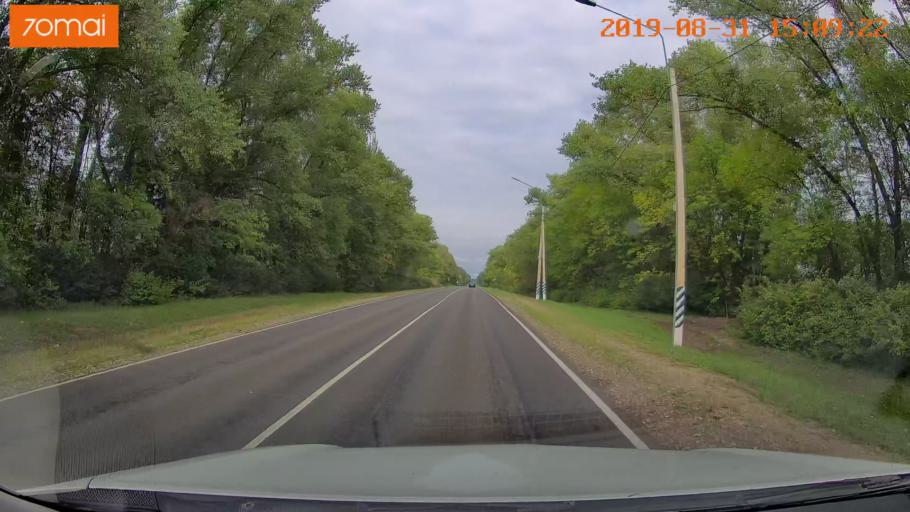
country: RU
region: Kaluga
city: Spas-Demensk
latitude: 54.4012
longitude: 34.1996
